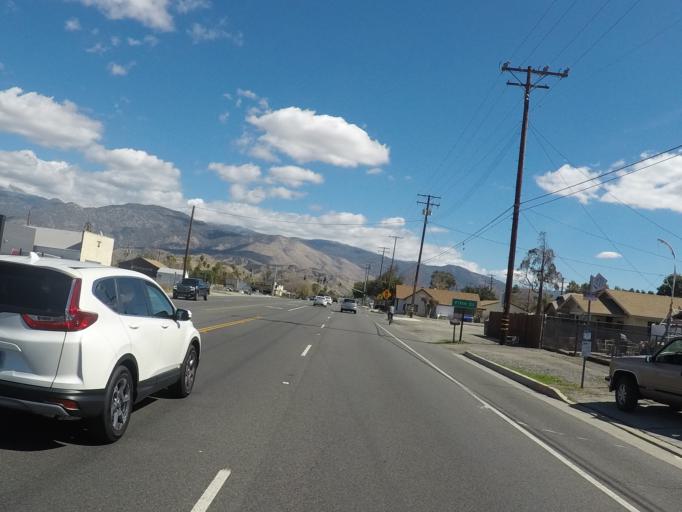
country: US
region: California
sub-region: Riverside County
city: Valle Vista
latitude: 33.7478
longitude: -116.8953
